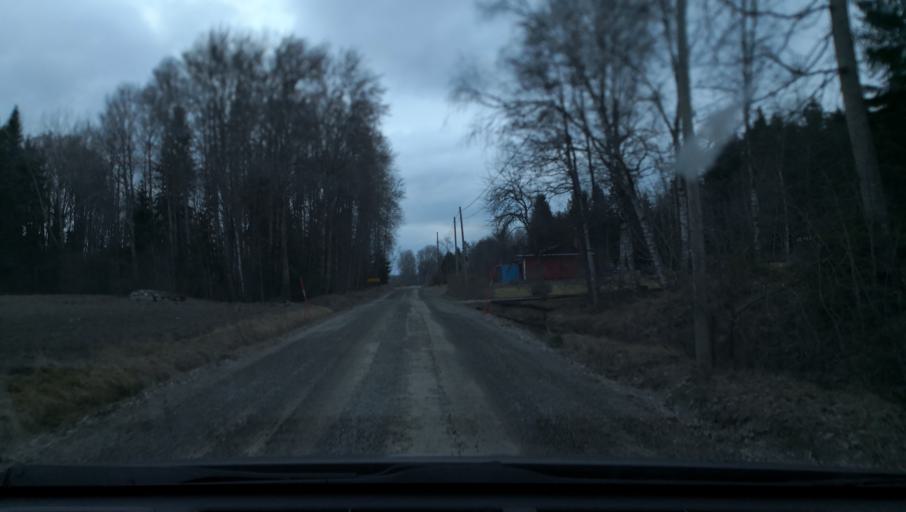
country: SE
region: Vaestmanland
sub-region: Kopings Kommun
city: Kolsva
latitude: 59.5819
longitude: 15.7138
